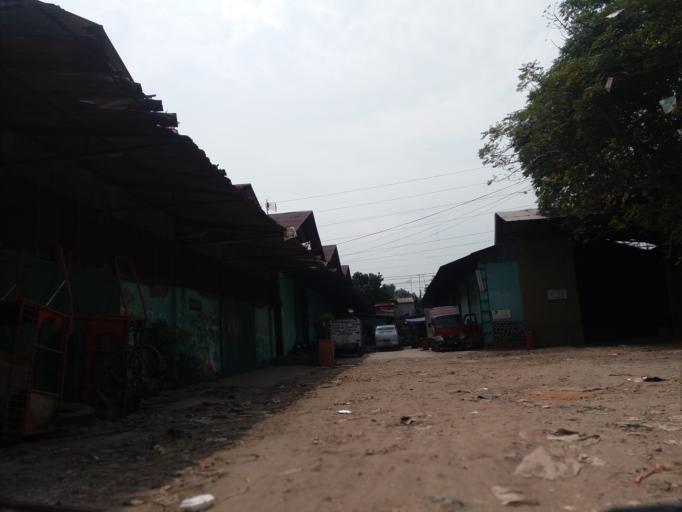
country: ID
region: Jakarta Raya
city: Jakarta
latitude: -6.1310
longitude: 106.8135
